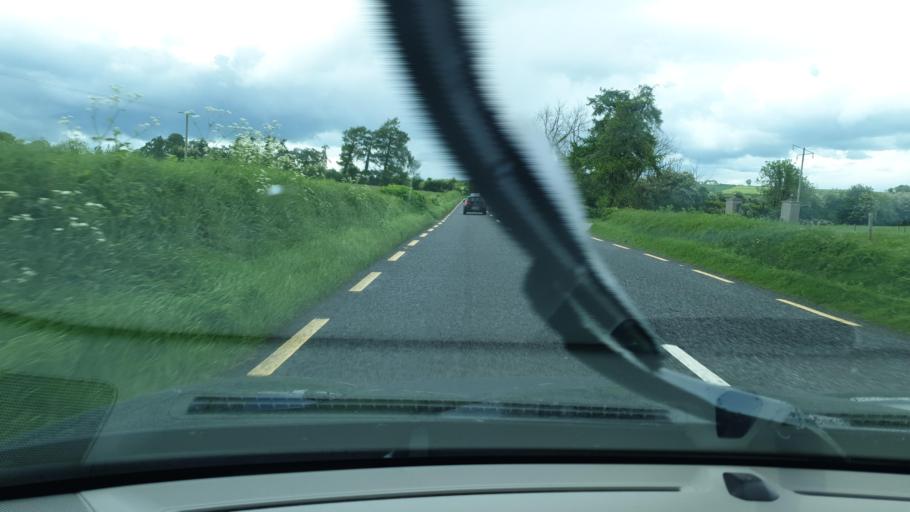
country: IE
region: Leinster
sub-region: Laois
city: Mountmellick
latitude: 53.1863
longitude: -7.4018
